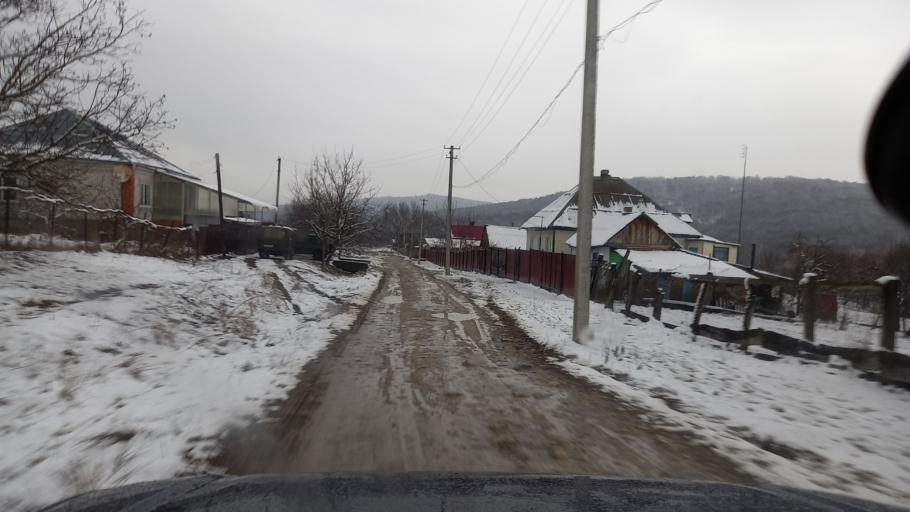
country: RU
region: Adygeya
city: Abadzekhskaya
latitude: 44.3543
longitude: 40.4135
